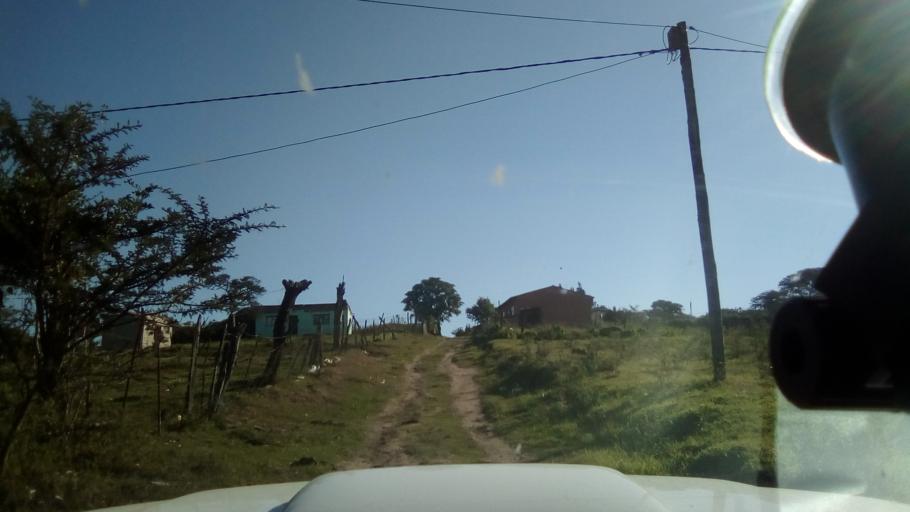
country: ZA
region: Eastern Cape
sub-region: Buffalo City Metropolitan Municipality
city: Bhisho
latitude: -32.7980
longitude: 27.3416
